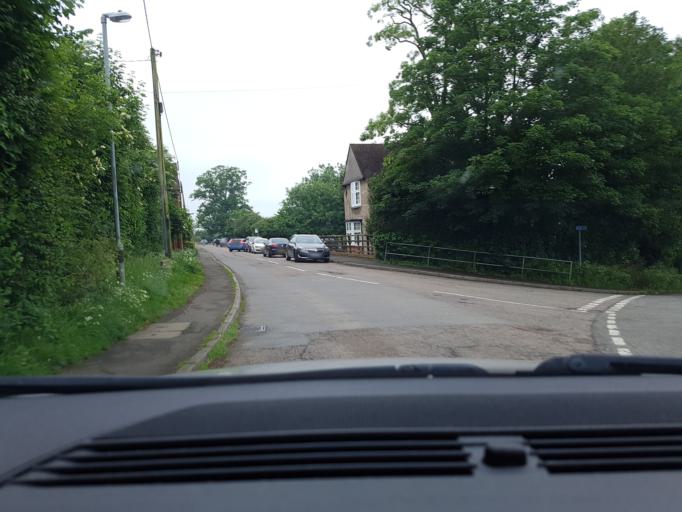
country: GB
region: England
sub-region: Buckinghamshire
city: Steeple Claydon
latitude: 51.9364
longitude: -0.9830
